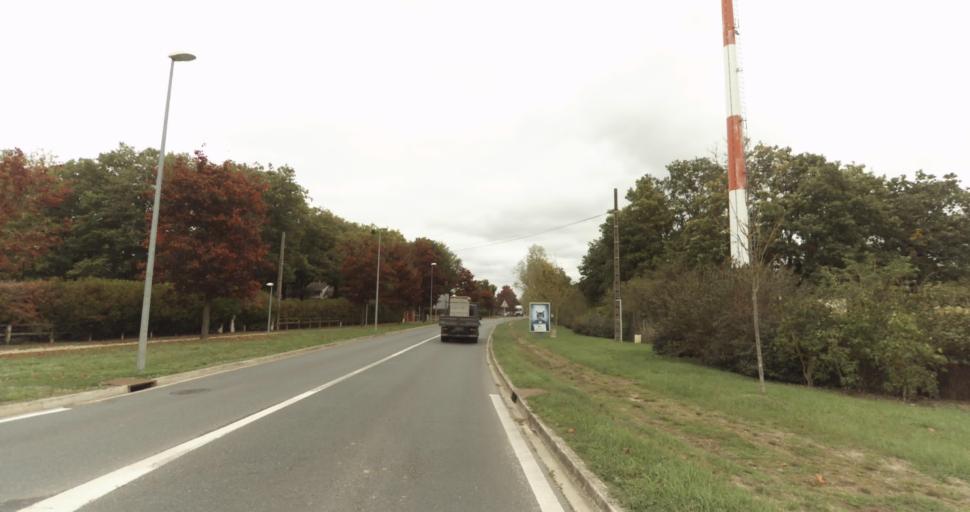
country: FR
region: Centre
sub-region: Departement d'Eure-et-Loir
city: Vernouillet
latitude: 48.7089
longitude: 1.3577
